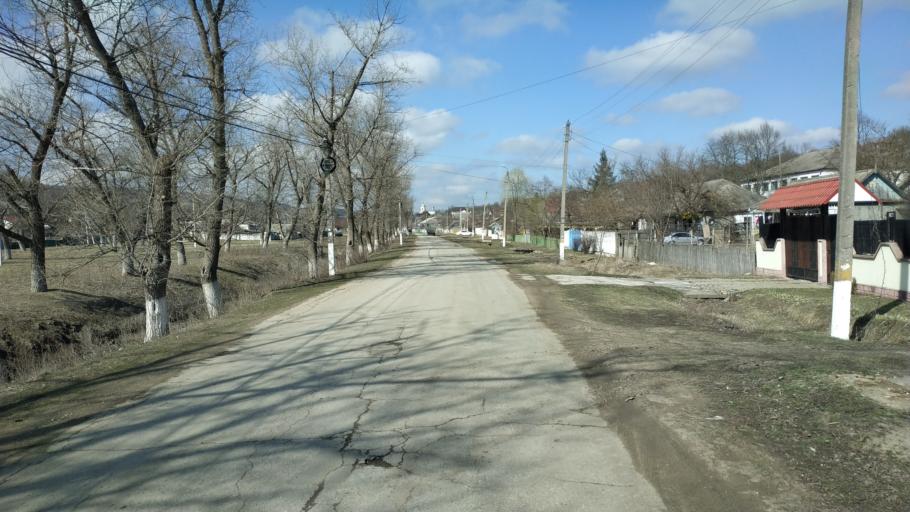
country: MD
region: Hincesti
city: Hincesti
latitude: 46.8776
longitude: 28.6279
